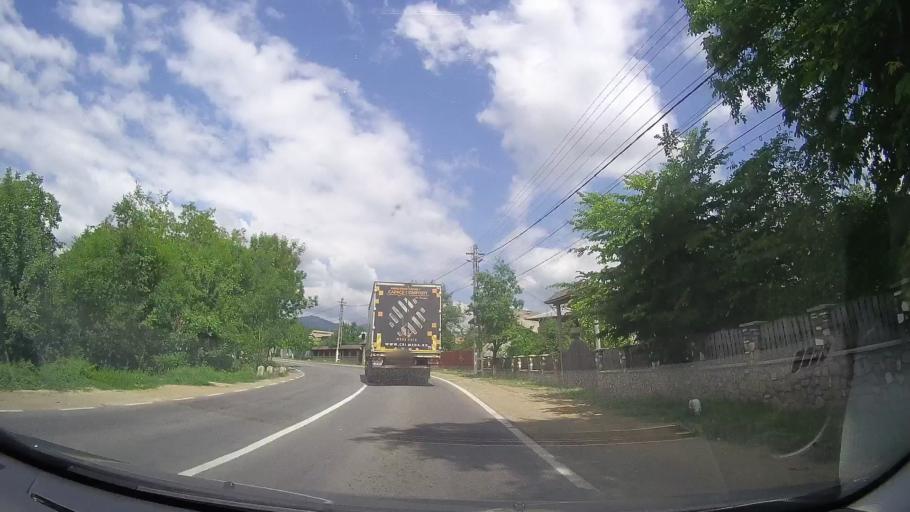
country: RO
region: Prahova
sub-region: Comuna Izvoarele
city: Homoraciu
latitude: 45.2773
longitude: 26.0114
